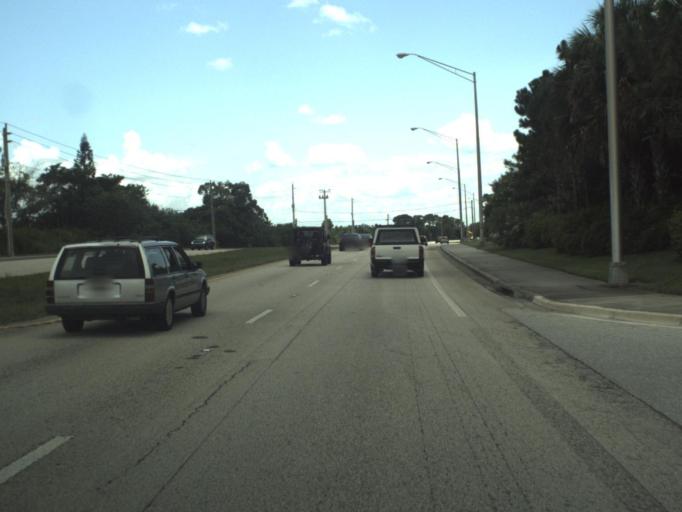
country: US
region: Florida
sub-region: Martin County
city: Palm City
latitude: 27.1543
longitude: -80.2454
